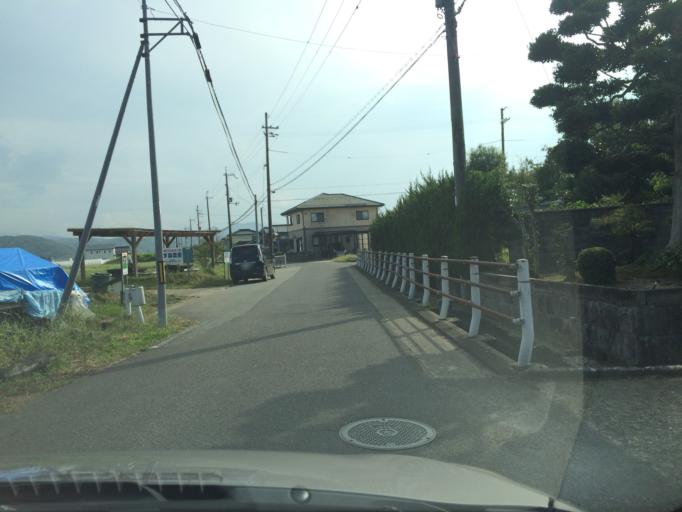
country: JP
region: Hyogo
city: Toyooka
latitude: 35.5215
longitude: 134.8269
